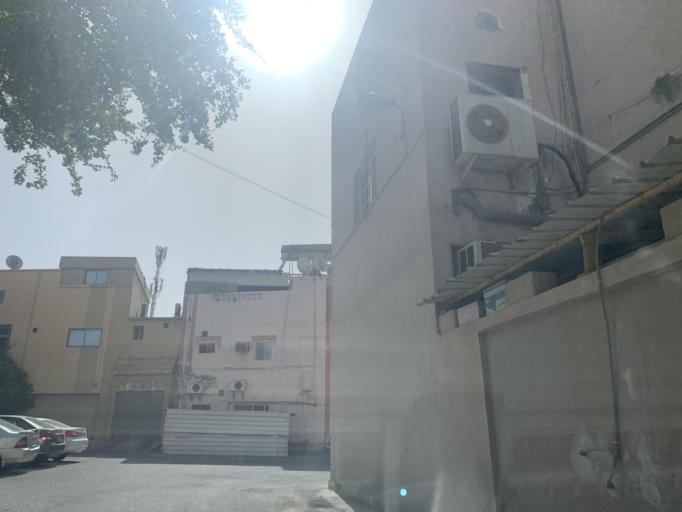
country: BH
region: Manama
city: Jidd Hafs
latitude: 26.2044
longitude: 50.5507
